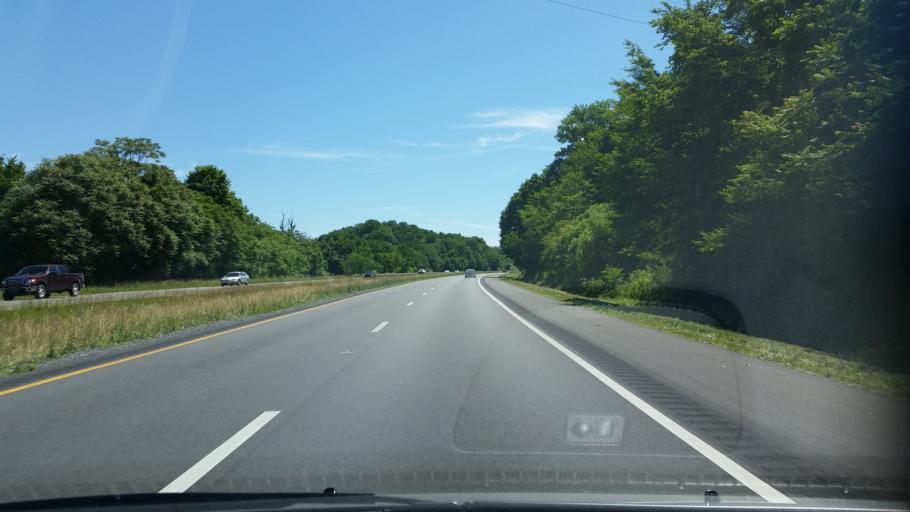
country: US
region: Virginia
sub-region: Smyth County
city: Marion
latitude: 36.8209
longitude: -81.5447
